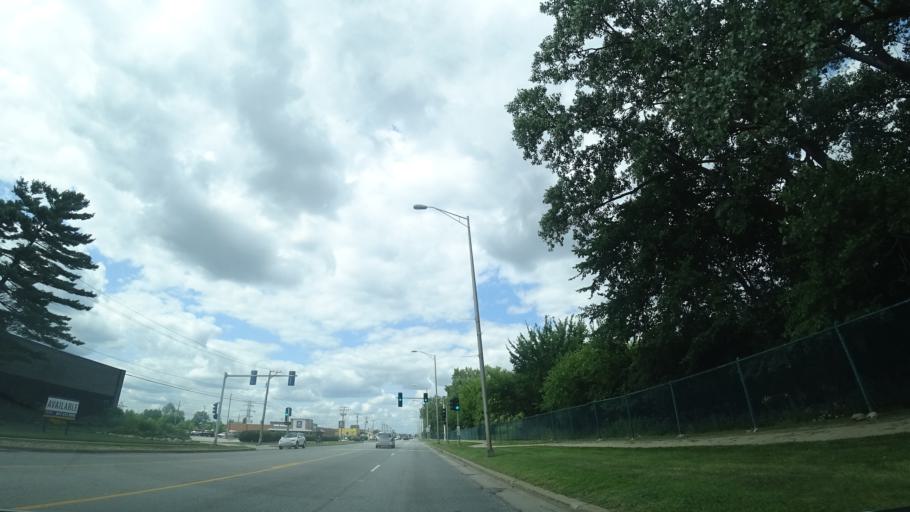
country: US
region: Illinois
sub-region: Cook County
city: Alsip
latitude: 41.6861
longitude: -87.7395
